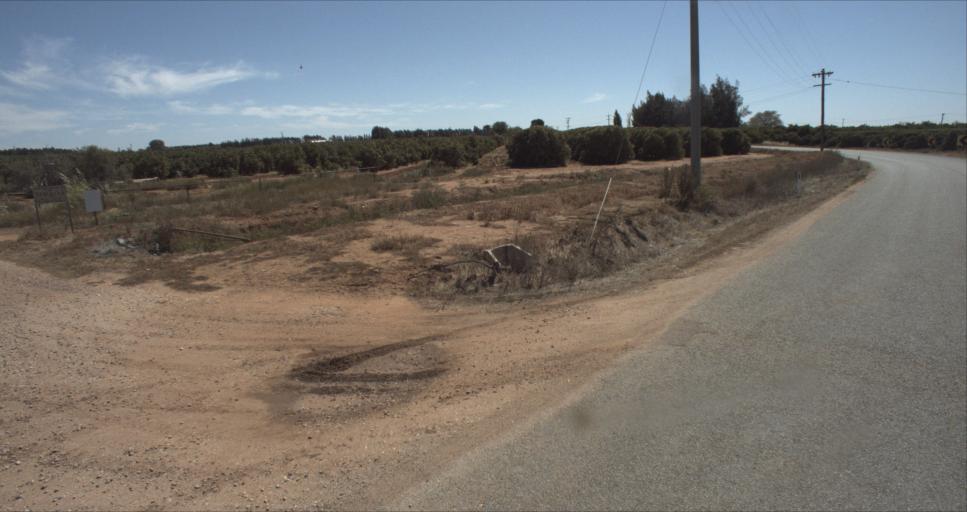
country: AU
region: New South Wales
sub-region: Leeton
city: Leeton
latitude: -34.5344
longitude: 146.3560
